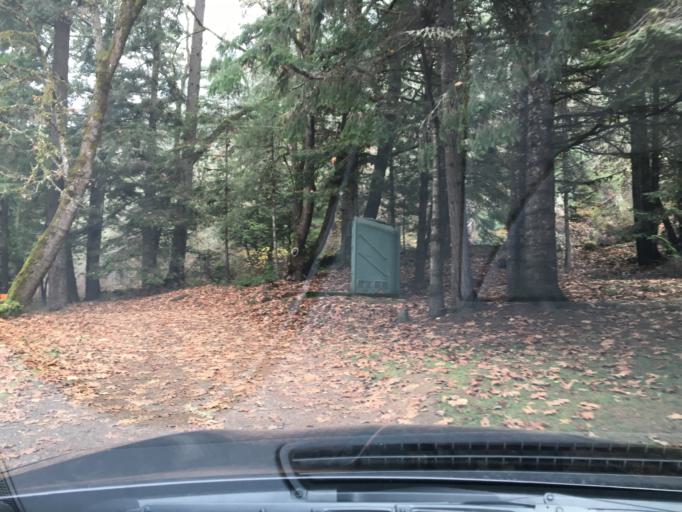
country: US
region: Oregon
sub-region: Douglas County
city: Sutherlin
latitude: 43.3834
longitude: -123.5260
